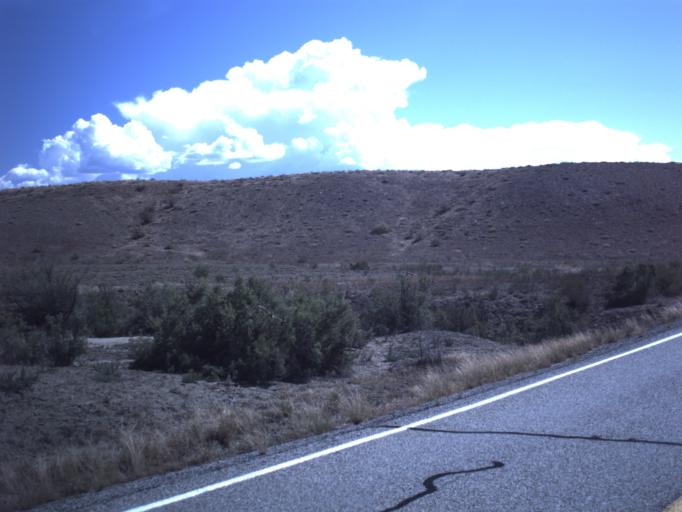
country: US
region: Utah
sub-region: Grand County
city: Moab
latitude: 38.8752
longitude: -109.3060
